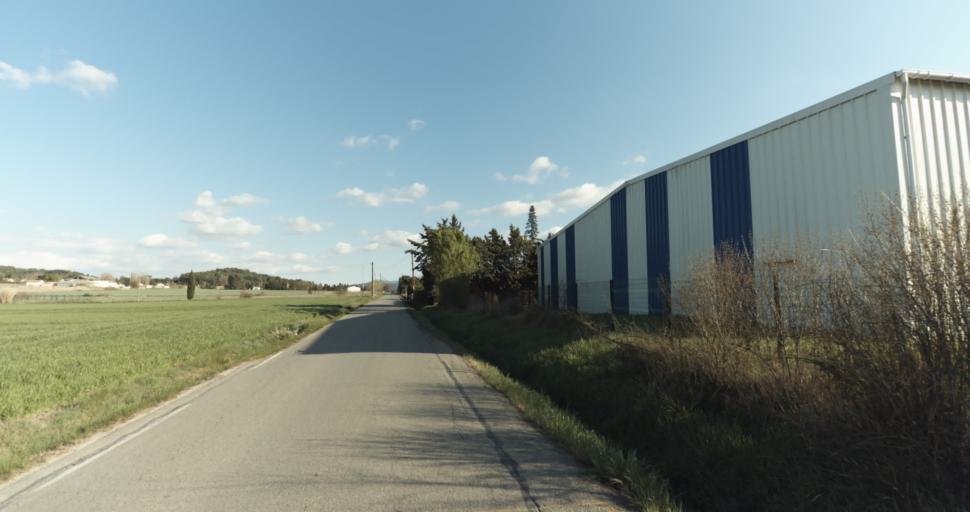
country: FR
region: Provence-Alpes-Cote d'Azur
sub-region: Departement des Bouches-du-Rhone
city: Cabries
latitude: 43.4937
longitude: 5.3801
